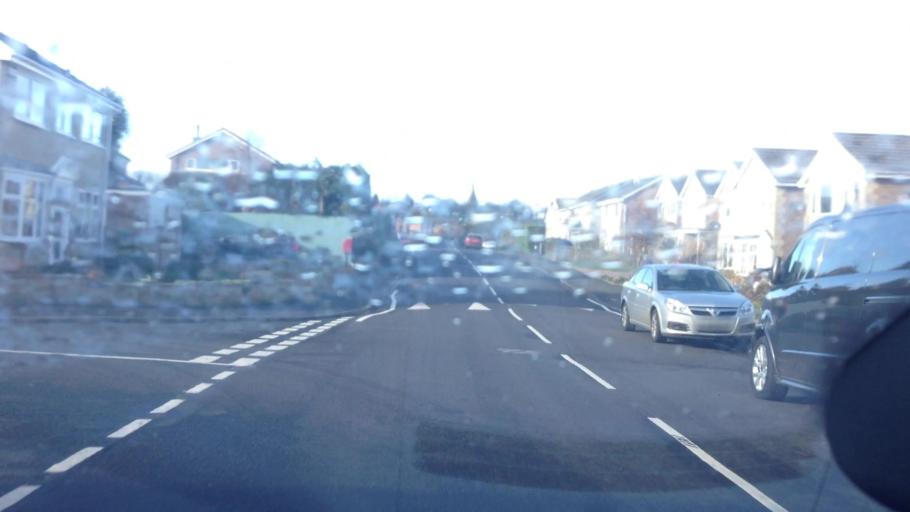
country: GB
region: England
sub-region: North Yorkshire
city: Knaresborough
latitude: 54.0017
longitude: -1.4528
